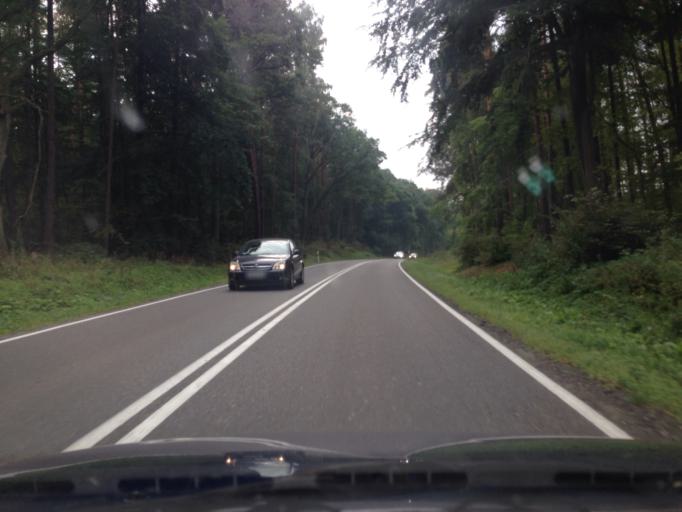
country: PL
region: Pomeranian Voivodeship
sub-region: Powiat kwidzynski
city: Ryjewo
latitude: 53.8162
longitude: 18.9784
